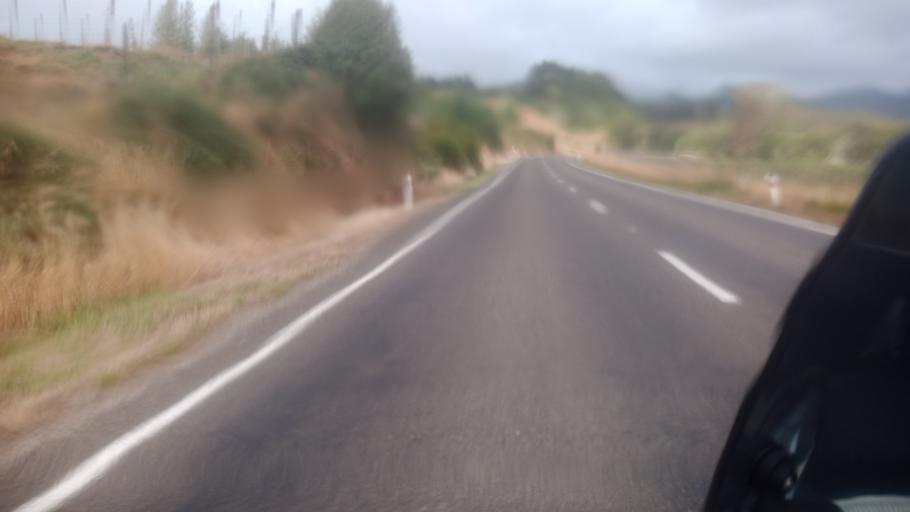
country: NZ
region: Bay of Plenty
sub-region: Opotiki District
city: Opotiki
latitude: -38.3636
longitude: 177.5195
